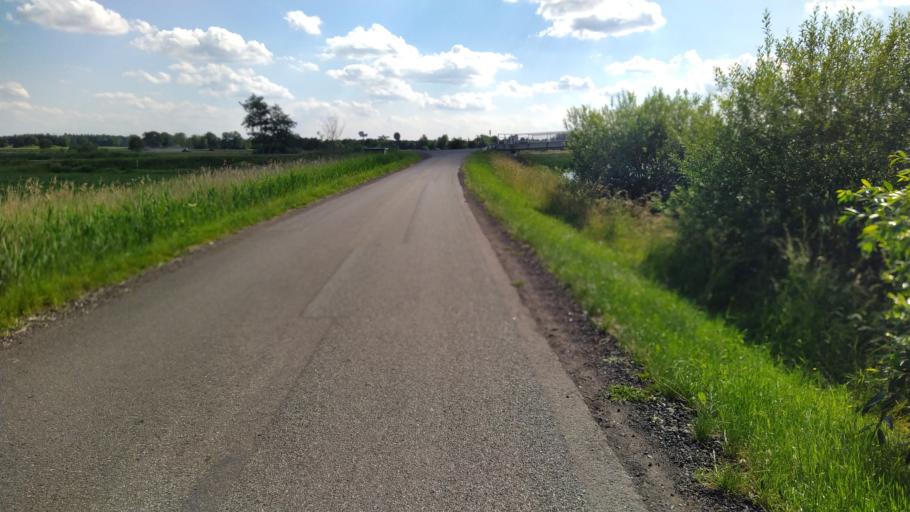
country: DE
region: Lower Saxony
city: Steinau
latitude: 53.6579
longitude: 8.8991
